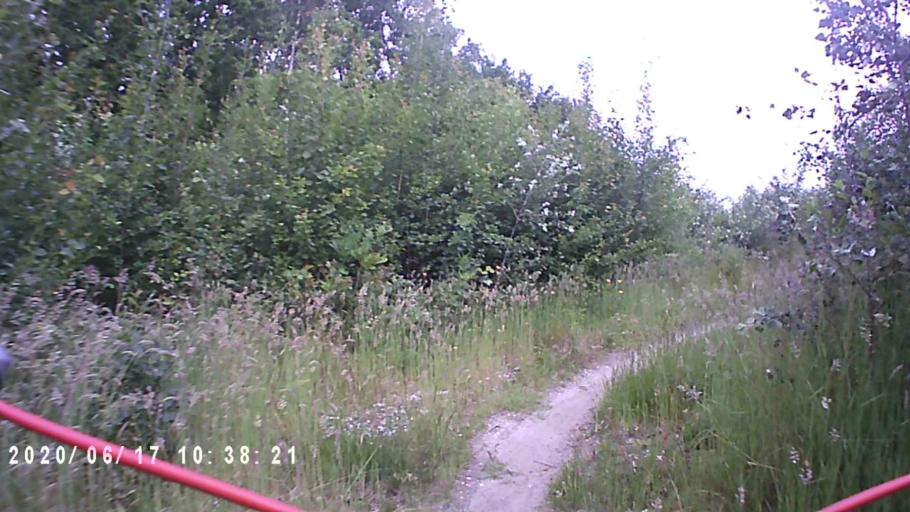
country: NL
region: Groningen
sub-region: Gemeente De Marne
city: Ulrum
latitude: 53.4006
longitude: 6.2332
